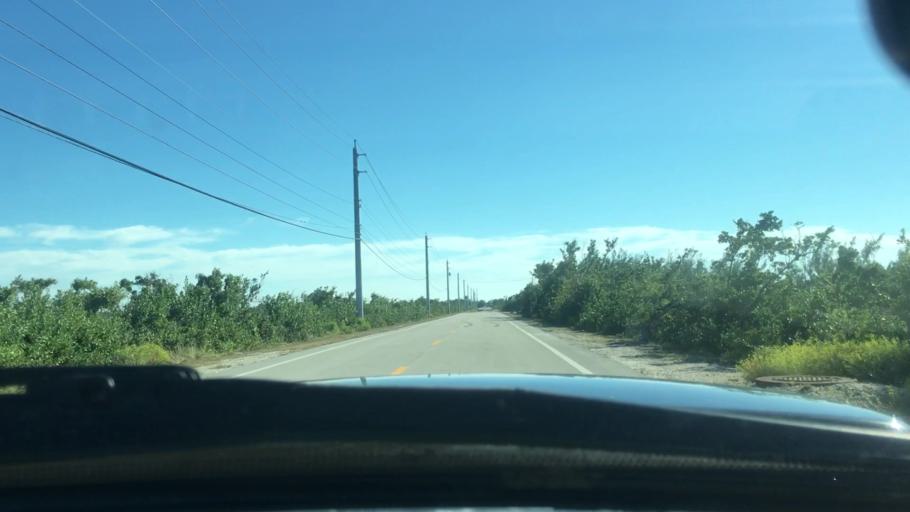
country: US
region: Florida
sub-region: Monroe County
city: Cudjoe Key
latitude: 24.6743
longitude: -81.4997
